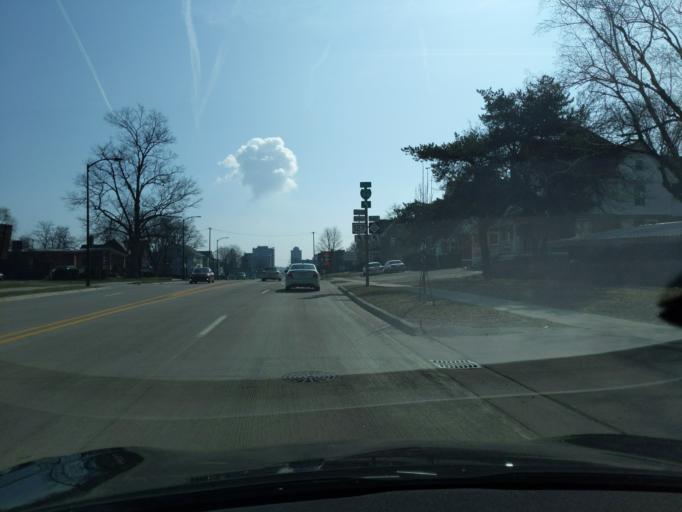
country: US
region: Michigan
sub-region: Jackson County
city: Jackson
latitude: 42.2474
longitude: -84.4196
